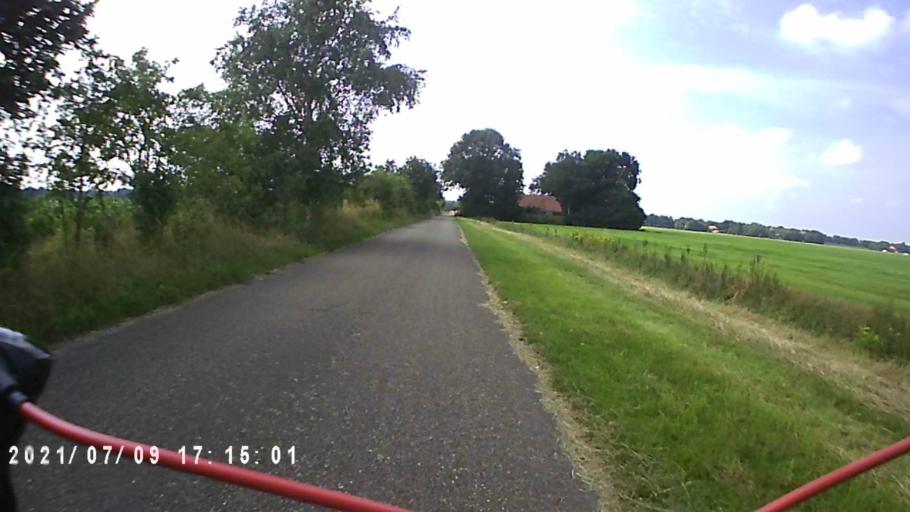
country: DE
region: Lower Saxony
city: Rhede
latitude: 53.0869
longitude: 7.1866
